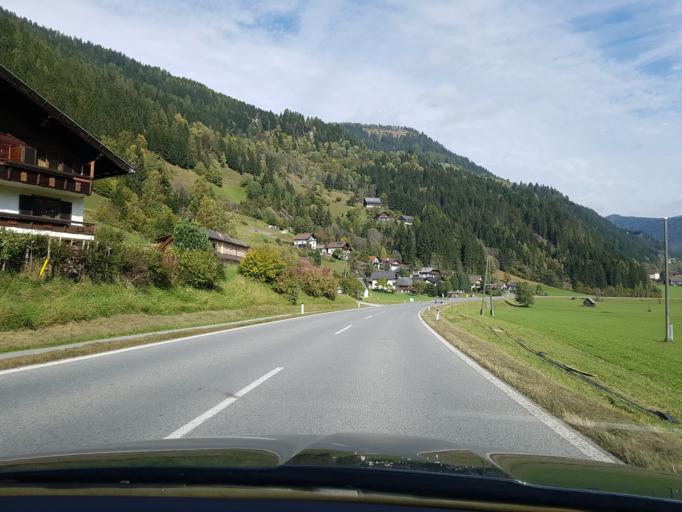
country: AT
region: Carinthia
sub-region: Politischer Bezirk Spittal an der Drau
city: Kleinkirchheim
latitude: 46.8312
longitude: 13.8620
